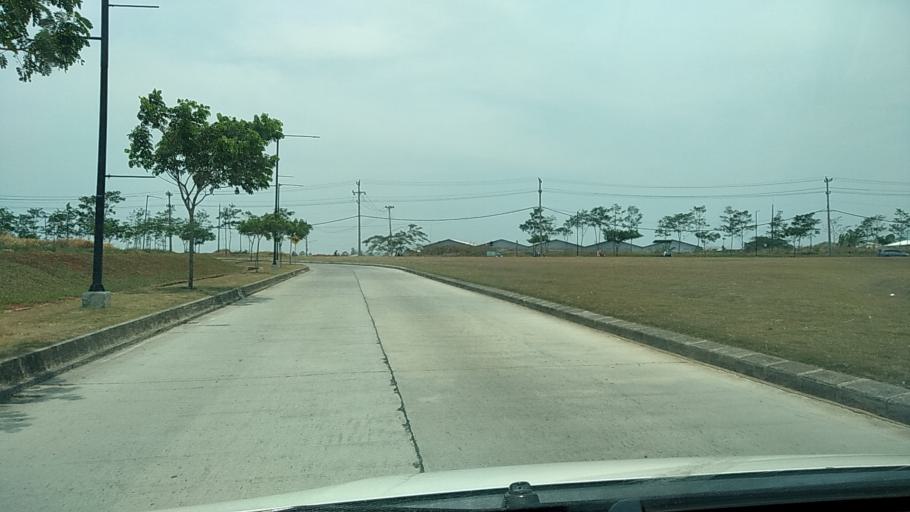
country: ID
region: Central Java
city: Semarang
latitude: -7.0403
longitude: 110.3289
